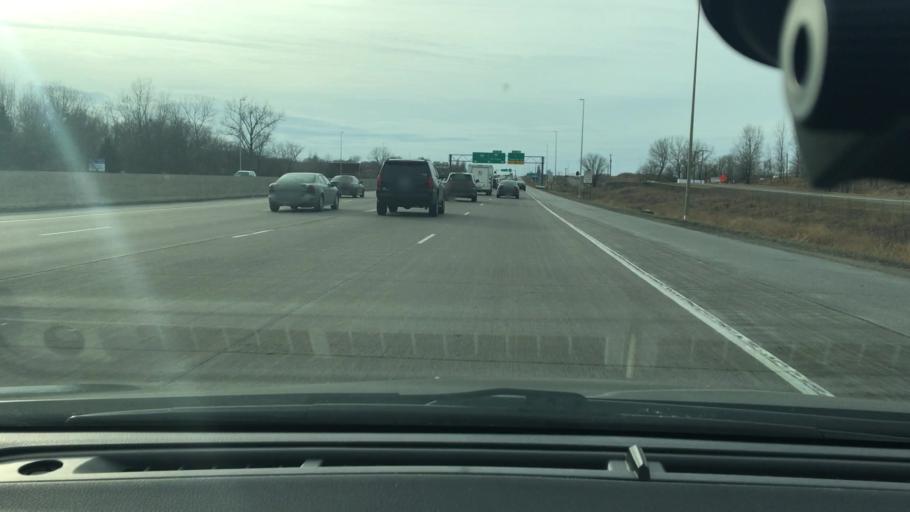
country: US
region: Minnesota
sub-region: Hennepin County
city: Osseo
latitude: 45.0855
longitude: -93.4095
